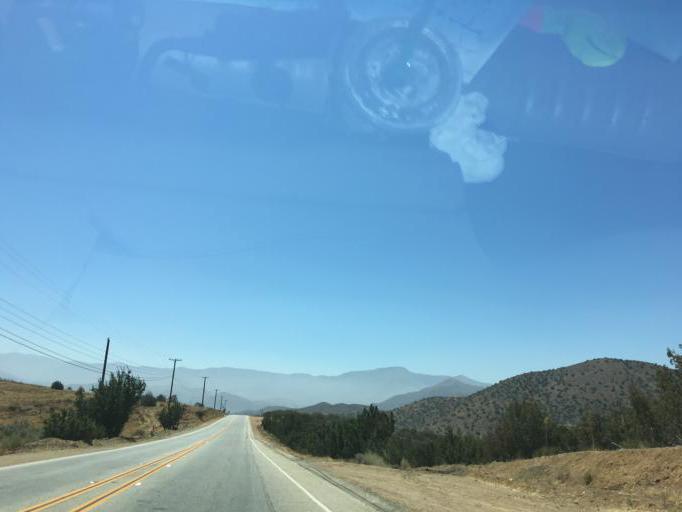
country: US
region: California
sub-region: Los Angeles County
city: Acton
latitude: 34.5076
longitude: -118.2326
